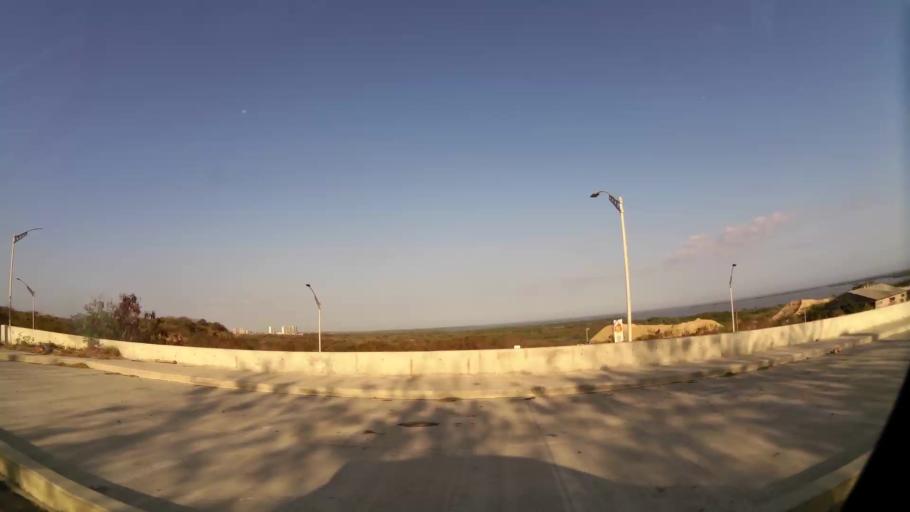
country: CO
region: Atlantico
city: Barranquilla
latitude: 11.0290
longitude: -74.8331
